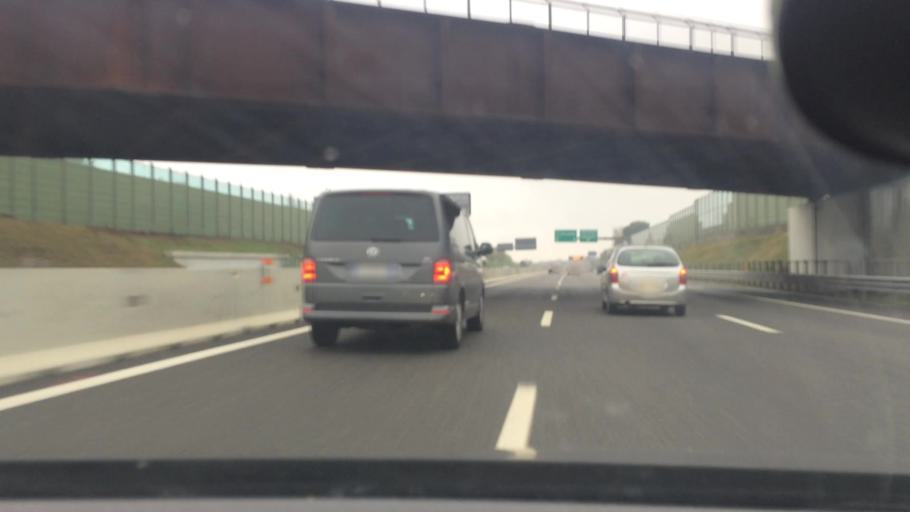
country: IT
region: Lombardy
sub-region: Provincia di Varese
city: Uboldo
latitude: 45.6174
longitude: 9.0130
